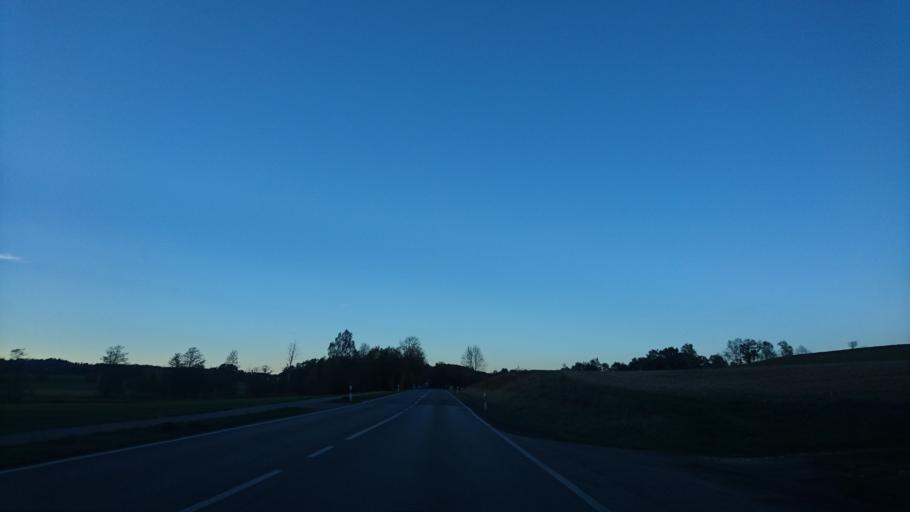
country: DE
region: Bavaria
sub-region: Swabia
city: Dinkelscherben
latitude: 48.3546
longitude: 10.5738
